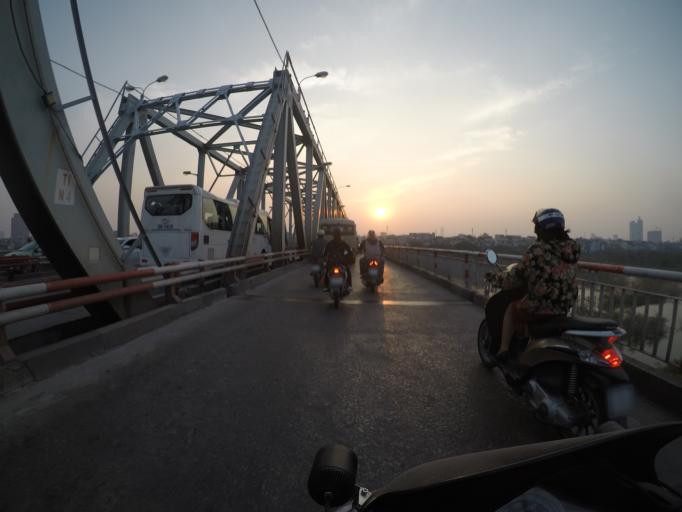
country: VN
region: Ha Noi
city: Hoan Kiem
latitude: 21.0373
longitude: 105.8594
